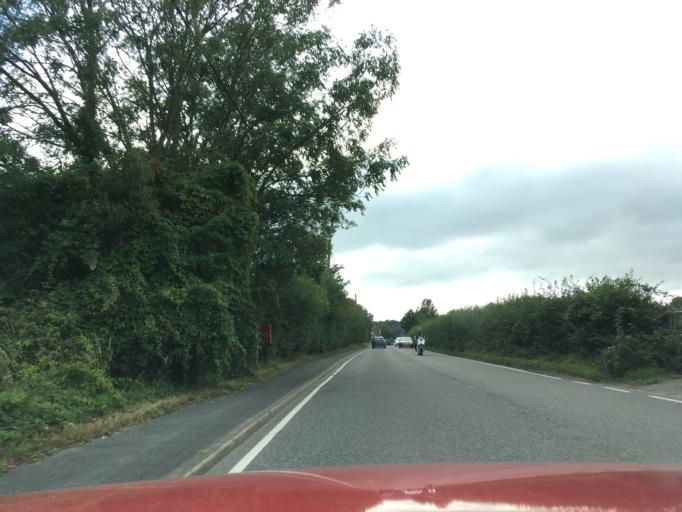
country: GB
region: England
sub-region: Hampshire
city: Petersfield
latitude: 51.0083
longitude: -0.9686
